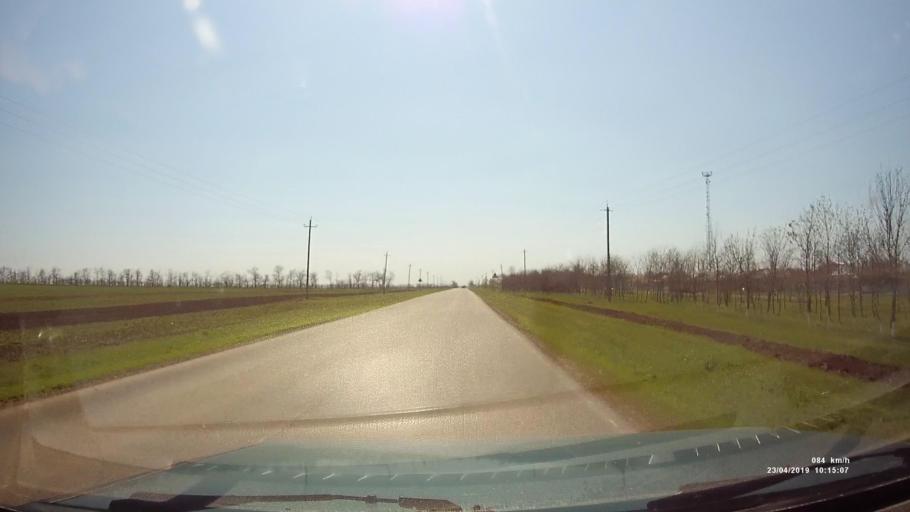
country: RU
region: Rostov
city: Sovetskoye
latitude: 46.6702
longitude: 42.3780
